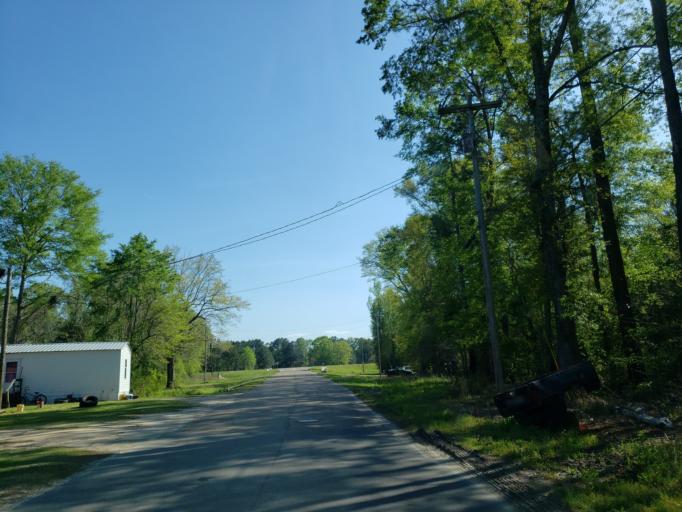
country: US
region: Mississippi
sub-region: Perry County
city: New Augusta
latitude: 31.1615
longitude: -88.9218
